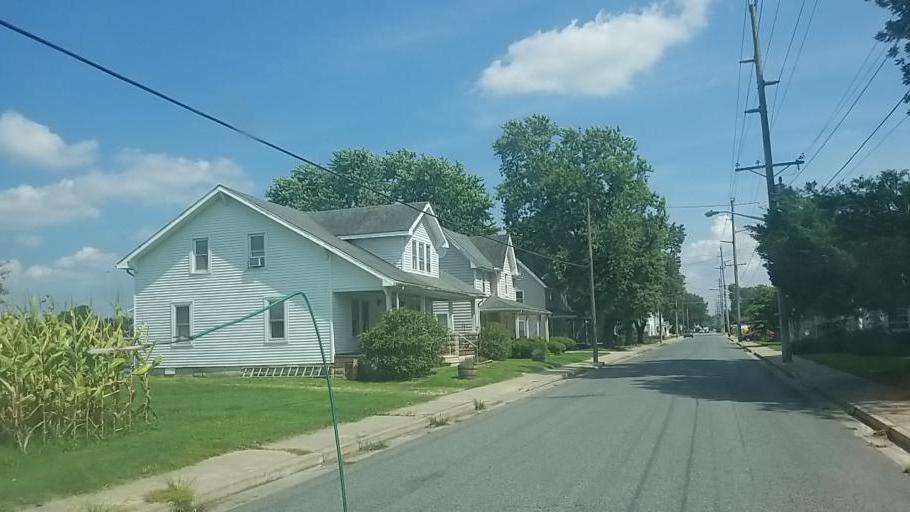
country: US
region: Maryland
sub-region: Wicomico County
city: Hebron
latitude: 38.4208
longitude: -75.6909
